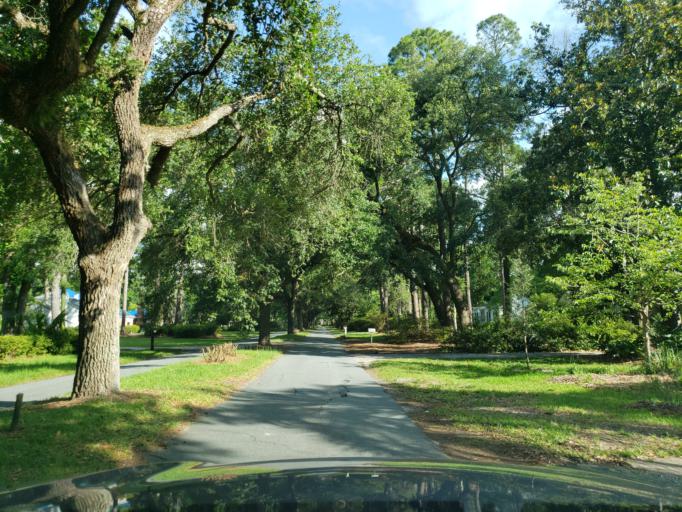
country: US
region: Georgia
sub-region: Chatham County
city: Isle of Hope
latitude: 31.9761
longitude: -81.0601
